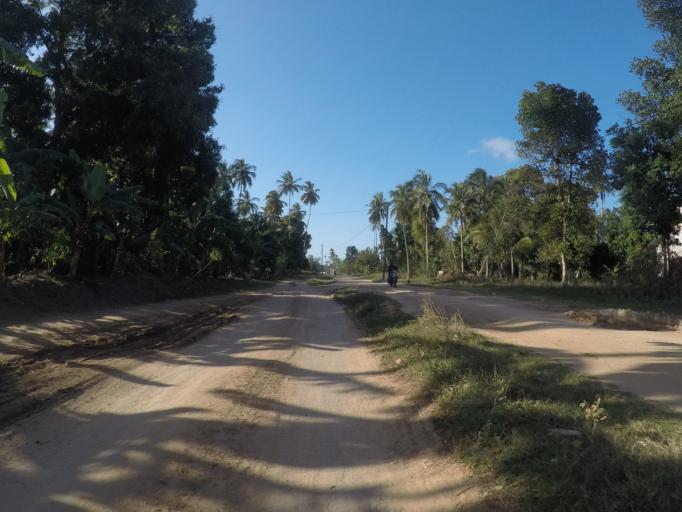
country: TZ
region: Zanzibar Central/South
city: Koani
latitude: -6.1591
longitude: 39.2873
